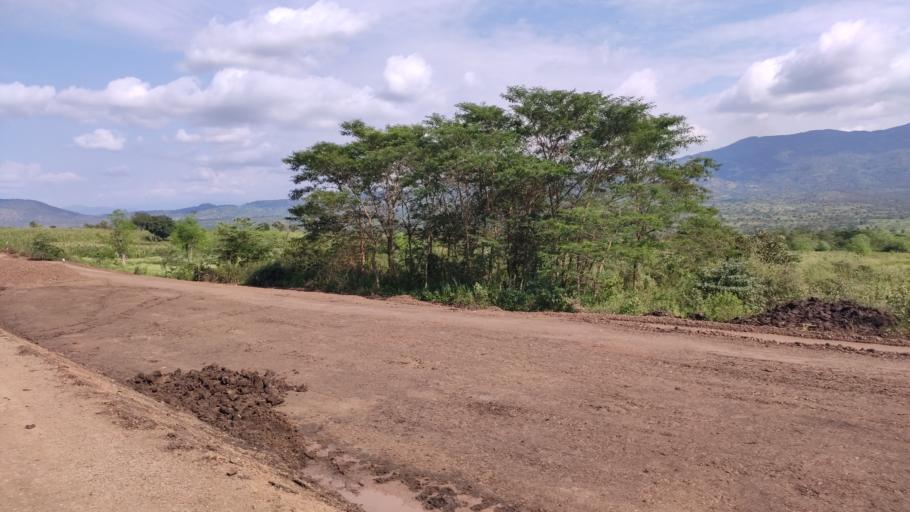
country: ET
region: Southern Nations, Nationalities, and People's Region
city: Felege Neway
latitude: 6.3971
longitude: 37.1112
